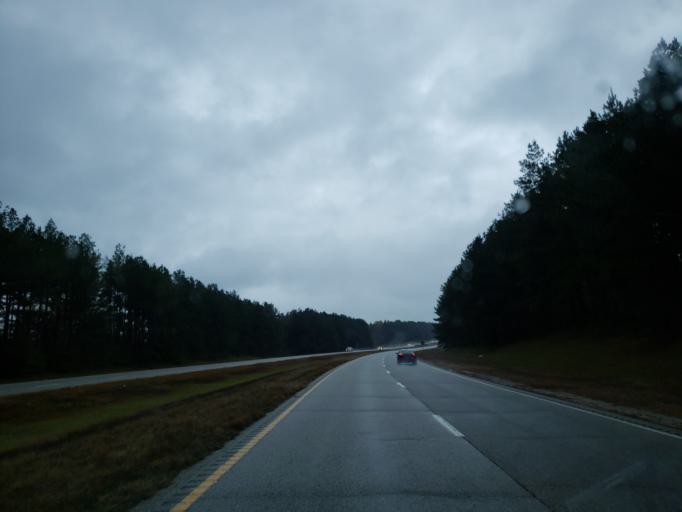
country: US
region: Mississippi
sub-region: Lauderdale County
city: Meridian
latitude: 32.2859
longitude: -88.6983
